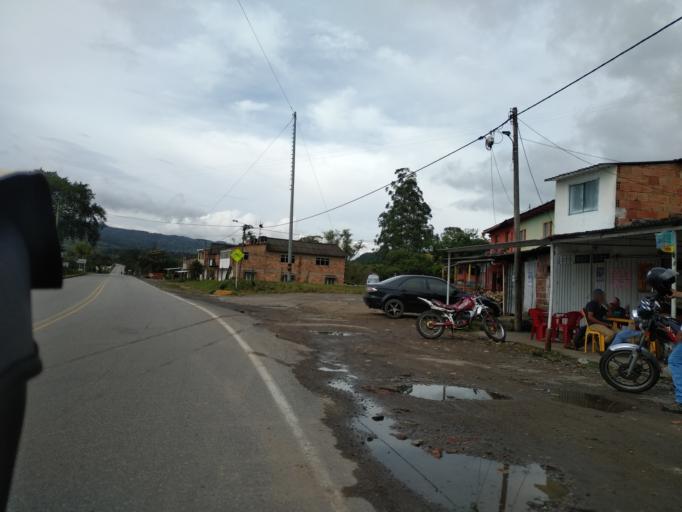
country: CO
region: Santander
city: Suaita
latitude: 6.1217
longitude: -73.3665
